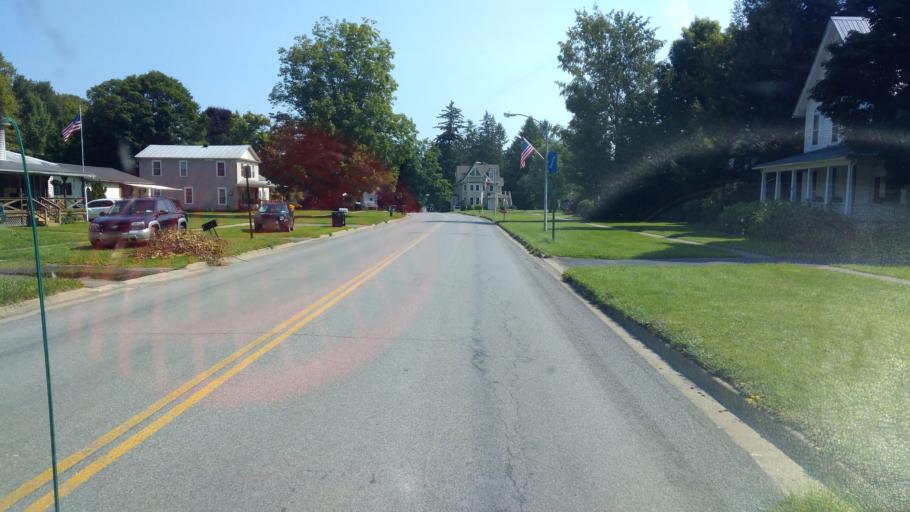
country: US
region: New York
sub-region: Allegany County
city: Friendship
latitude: 42.2089
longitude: -78.1317
